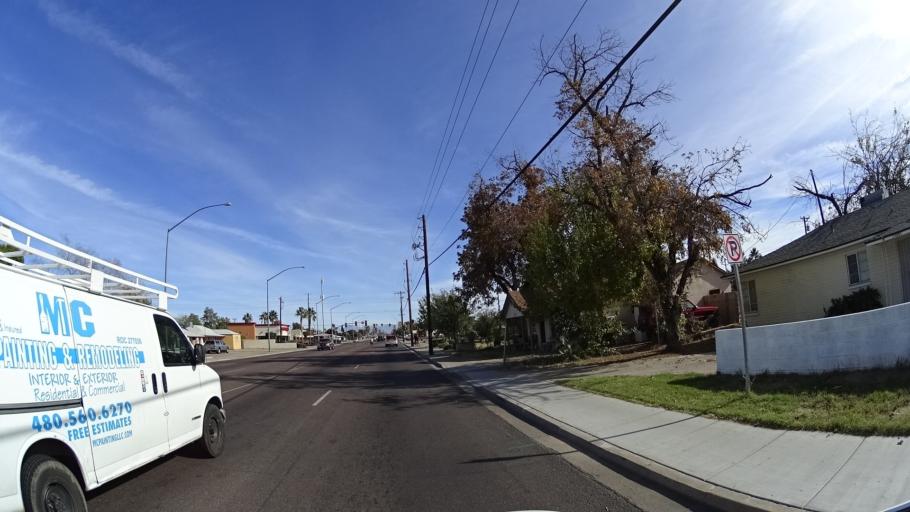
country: US
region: Arizona
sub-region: Maricopa County
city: Mesa
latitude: 33.4078
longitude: -111.8069
